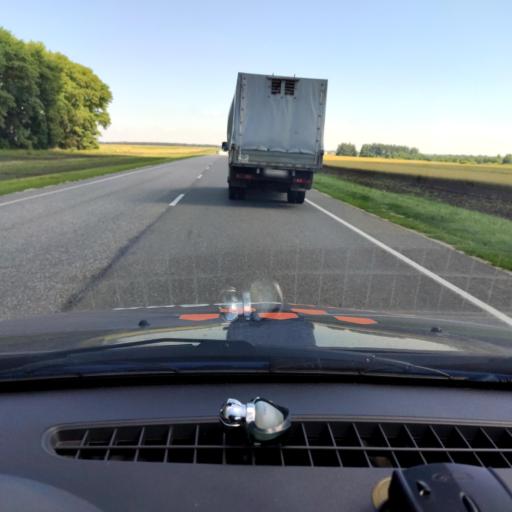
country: RU
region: Orjol
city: Pokrovskoye
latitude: 52.6378
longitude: 36.6813
